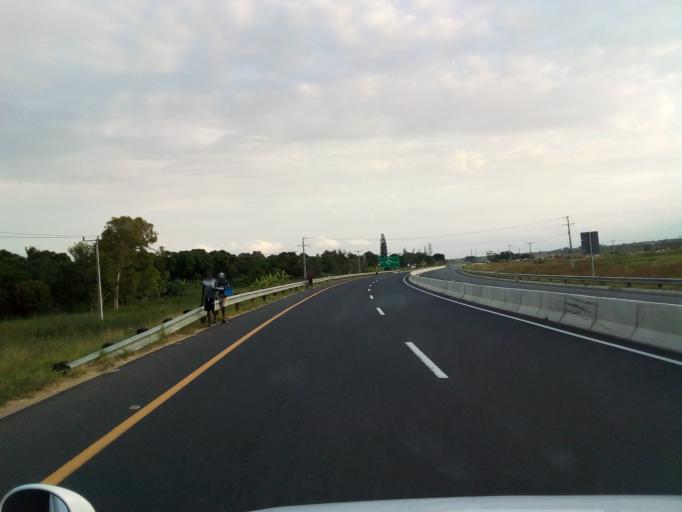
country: MZ
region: Maputo City
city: Maputo
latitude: -26.0023
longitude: 32.5582
